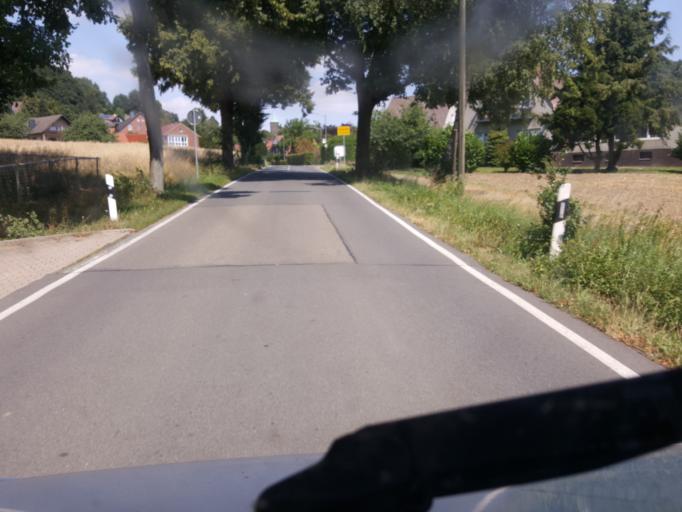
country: DE
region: North Rhine-Westphalia
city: Bad Oeynhausen
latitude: 52.2636
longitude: 8.7675
